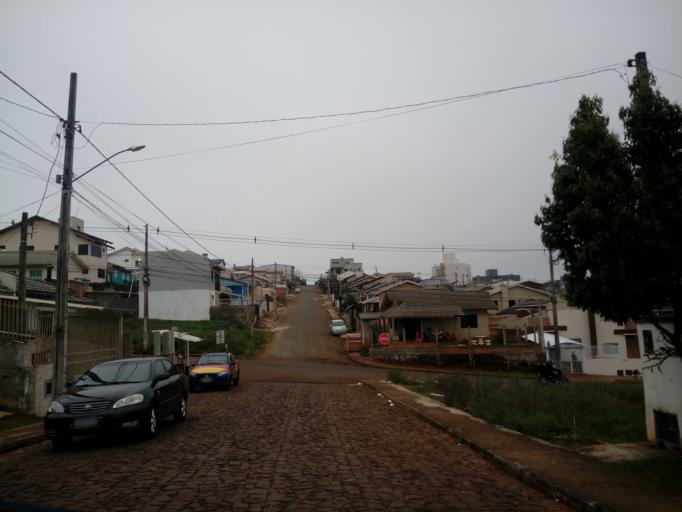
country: BR
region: Santa Catarina
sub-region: Chapeco
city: Chapeco
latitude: -27.1064
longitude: -52.6701
